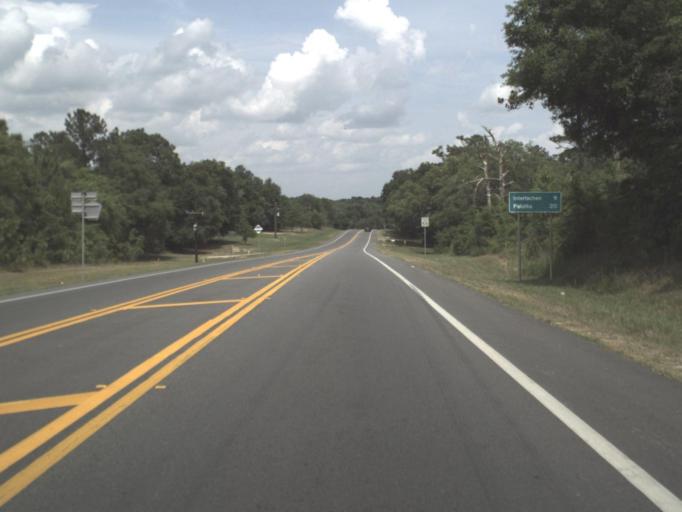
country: US
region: Florida
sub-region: Alachua County
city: Hawthorne
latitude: 29.6082
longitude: -82.0241
